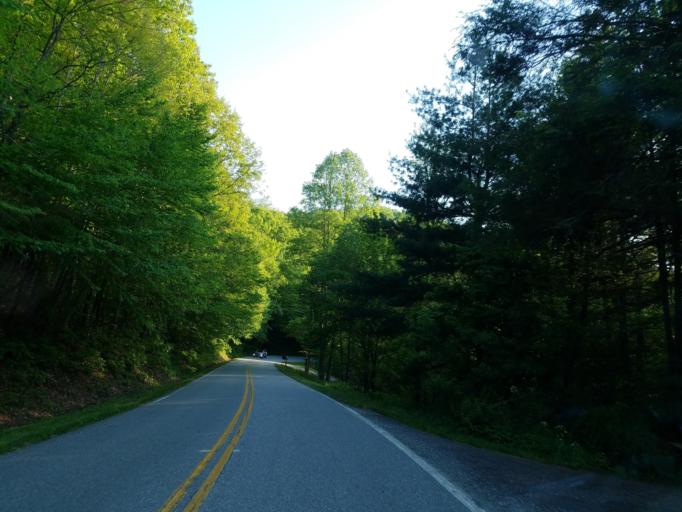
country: US
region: Georgia
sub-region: Lumpkin County
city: Dahlonega
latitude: 34.7035
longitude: -84.0446
